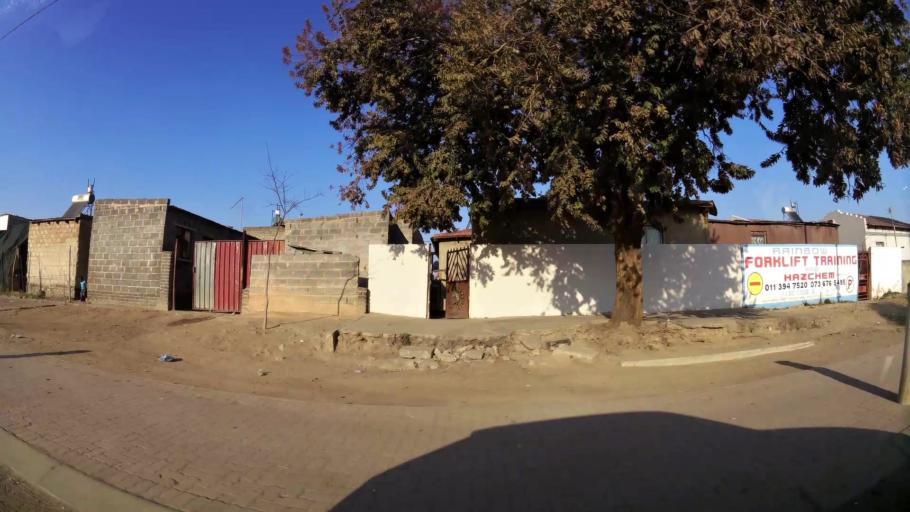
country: ZA
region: Gauteng
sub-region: Ekurhuleni Metropolitan Municipality
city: Tembisa
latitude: -25.9939
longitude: 28.1995
